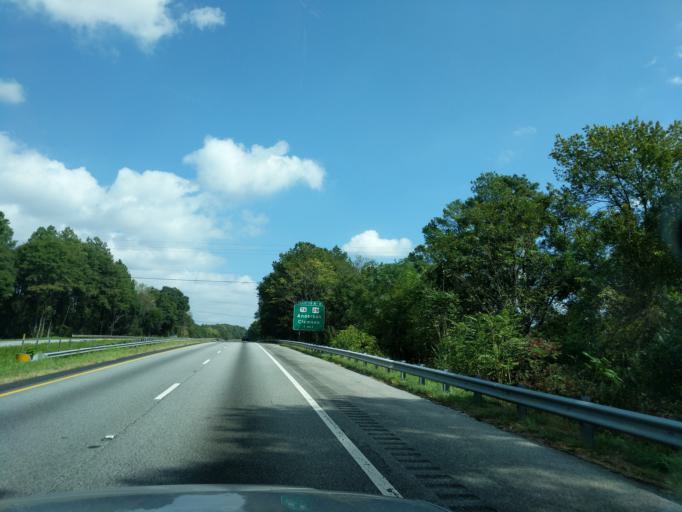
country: US
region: South Carolina
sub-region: Anderson County
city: Centerville
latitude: 34.5680
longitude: -82.7359
